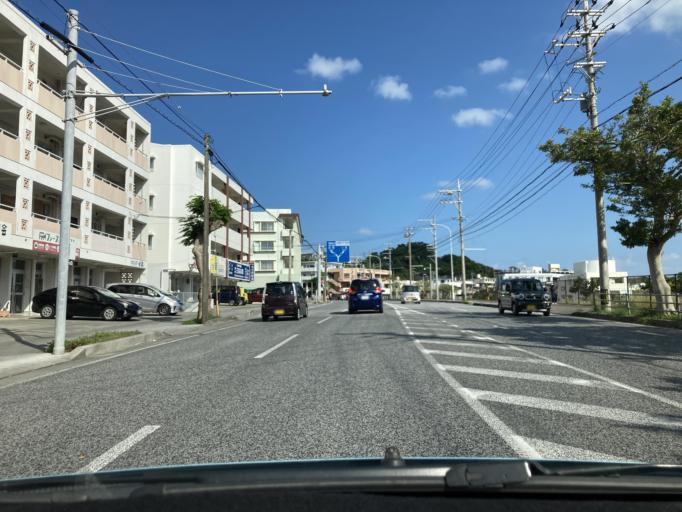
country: JP
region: Okinawa
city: Tomigusuku
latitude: 26.1802
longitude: 127.6811
